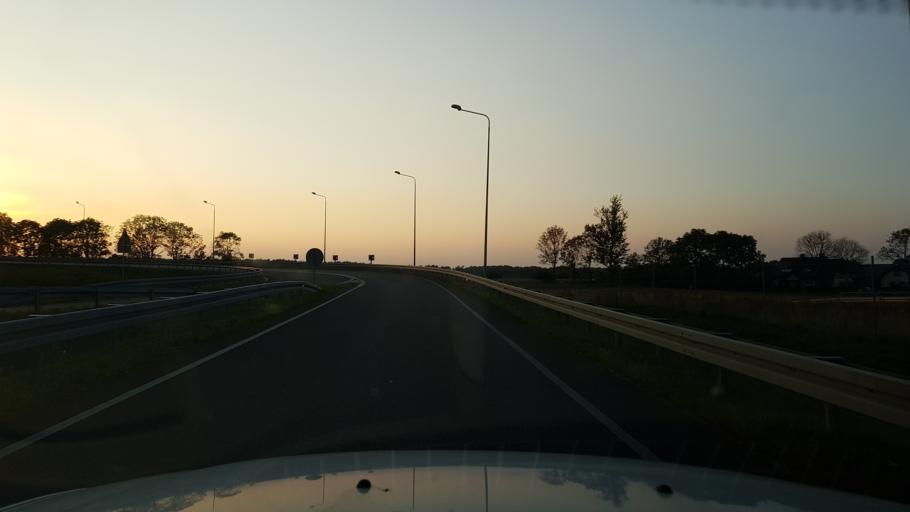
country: PL
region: West Pomeranian Voivodeship
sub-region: Powiat goleniowski
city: Nowogard
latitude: 53.6907
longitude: 15.1399
